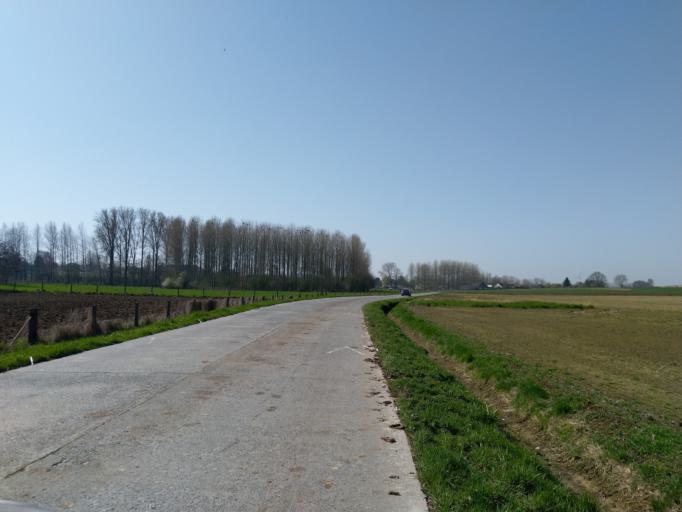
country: BE
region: Wallonia
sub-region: Province du Hainaut
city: Silly
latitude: 50.6738
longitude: 3.9138
